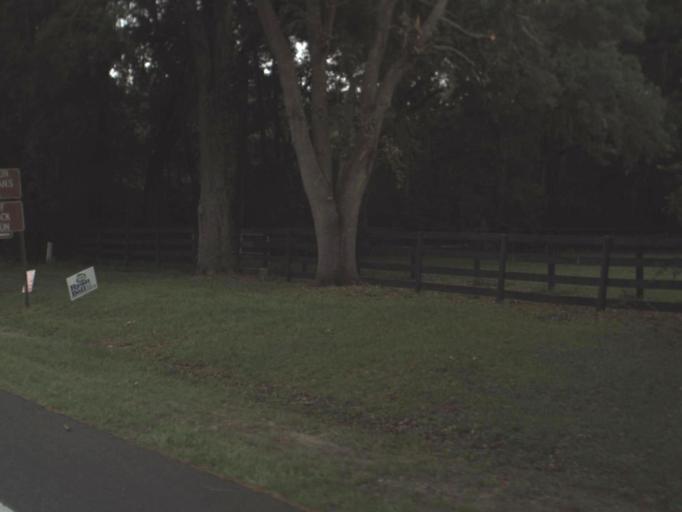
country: US
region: Florida
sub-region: Levy County
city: Williston
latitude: 29.3595
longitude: -82.4558
